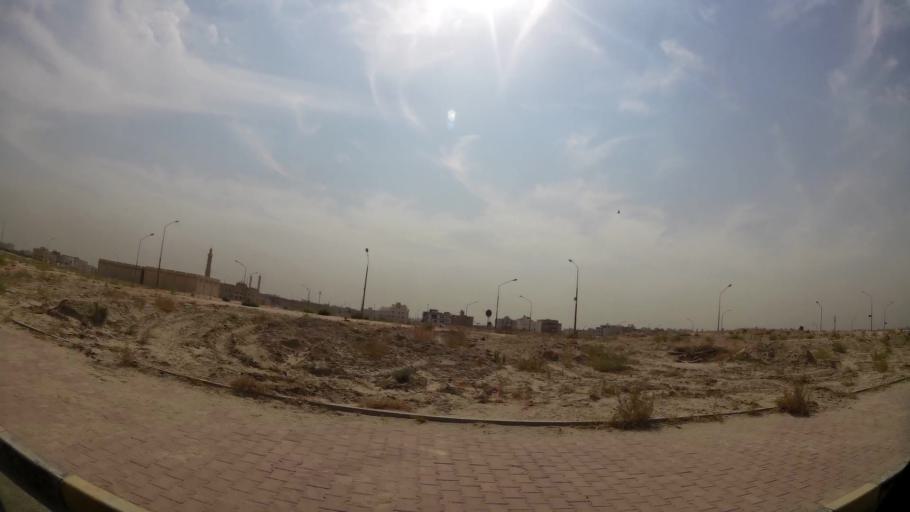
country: KW
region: Al Farwaniyah
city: Janub as Surrah
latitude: 29.2995
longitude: 47.9911
